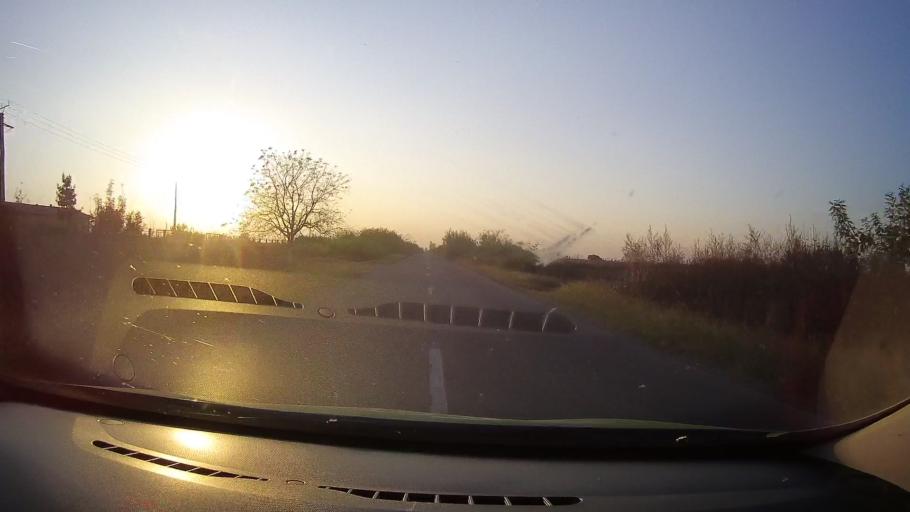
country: RO
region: Arad
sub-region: Comuna Ineu
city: Ineu
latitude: 46.4305
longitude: 21.8182
